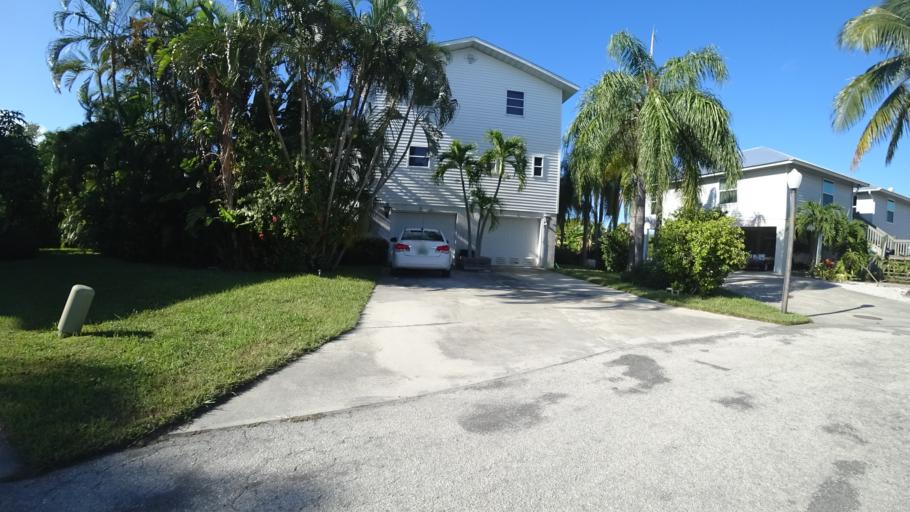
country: US
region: Florida
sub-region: Manatee County
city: Anna Maria
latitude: 27.5320
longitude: -82.7380
